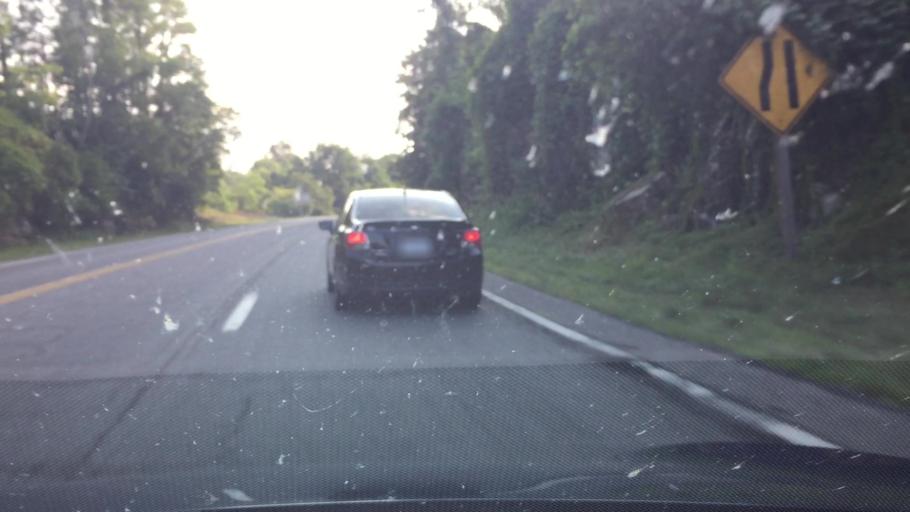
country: US
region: Virginia
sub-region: City of Radford
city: Radford
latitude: 37.1339
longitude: -80.6182
